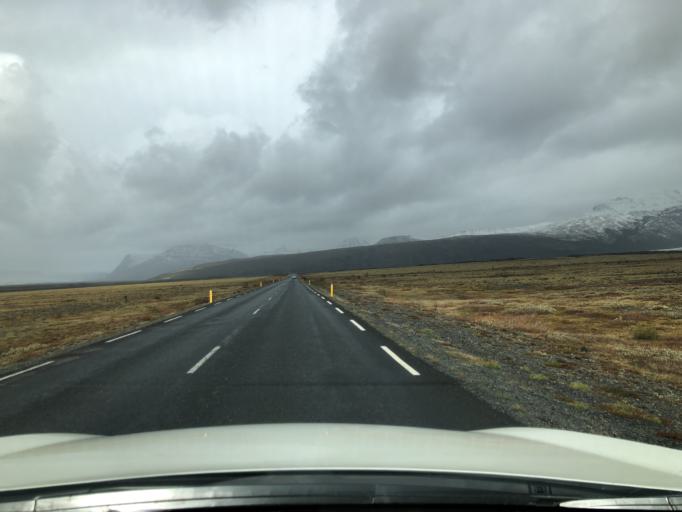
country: IS
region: East
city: Hoefn
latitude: 63.9948
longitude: -16.9042
